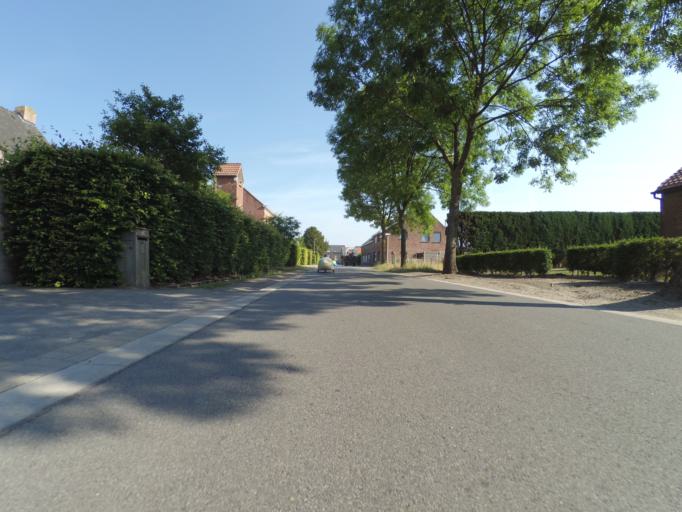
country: BE
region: Flanders
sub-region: Provincie Antwerpen
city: Essen
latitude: 51.4446
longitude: 4.4106
